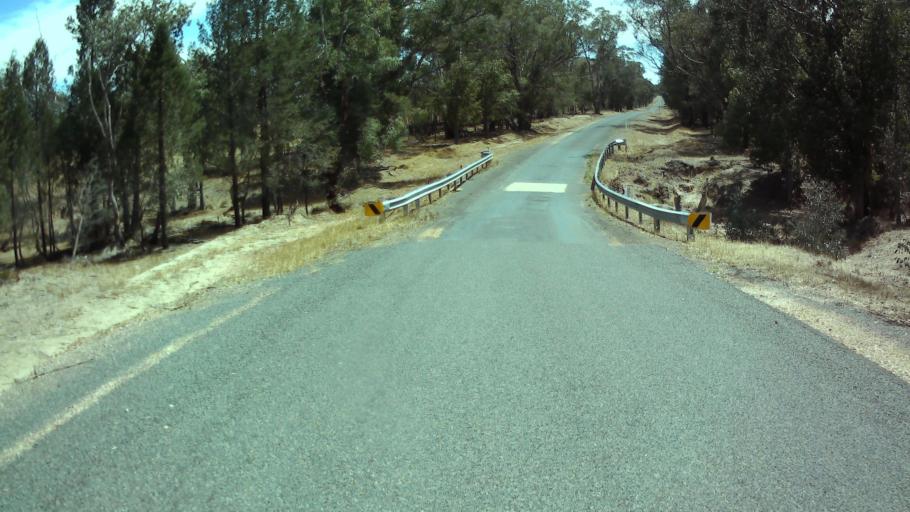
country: AU
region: New South Wales
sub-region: Weddin
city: Grenfell
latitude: -33.7675
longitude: 148.2042
